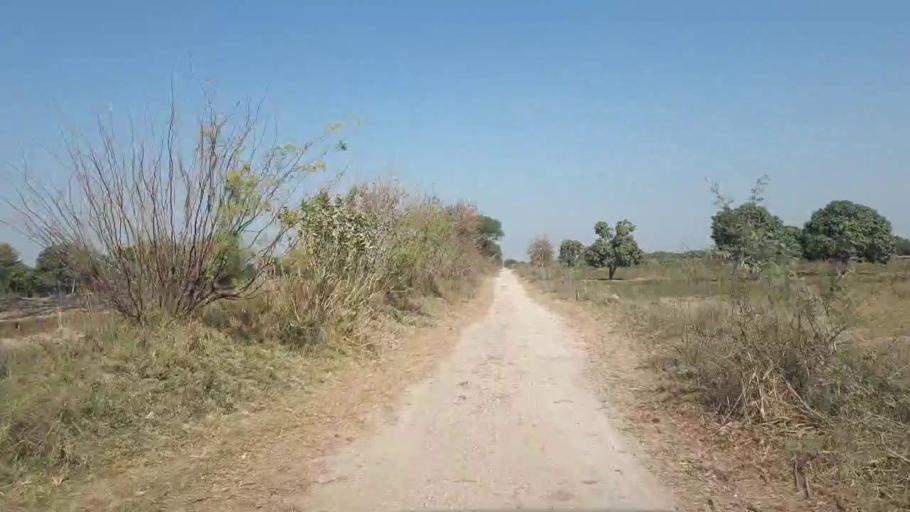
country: PK
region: Sindh
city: Chambar
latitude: 25.3018
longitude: 68.6927
